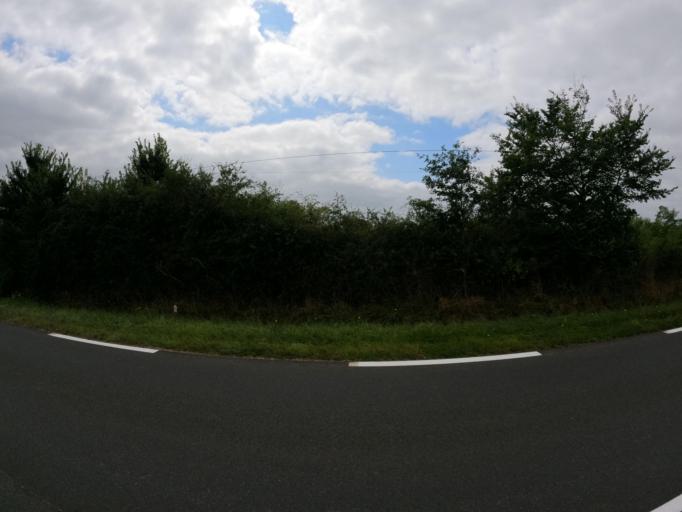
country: FR
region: Poitou-Charentes
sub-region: Departement de la Vienne
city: Charroux
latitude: 46.1281
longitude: 0.4851
